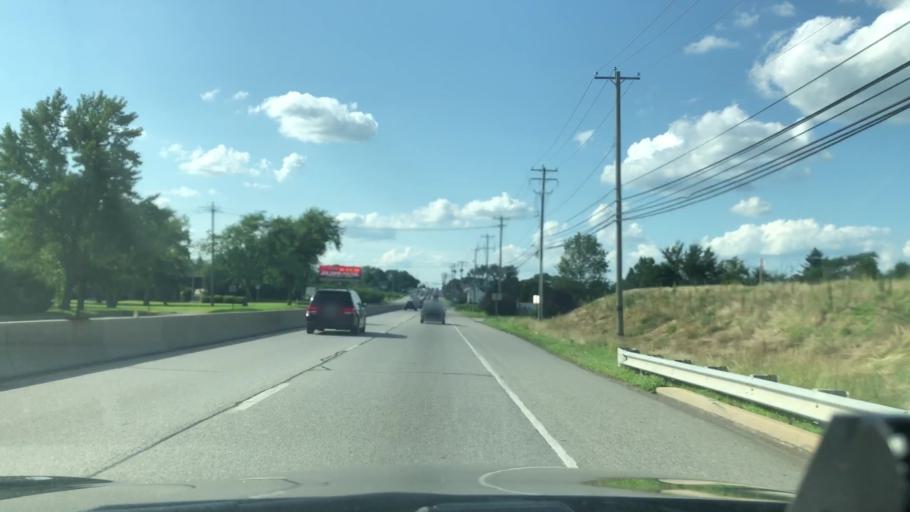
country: US
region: Pennsylvania
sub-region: Montgomery County
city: Spring House
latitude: 40.2120
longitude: -75.2255
